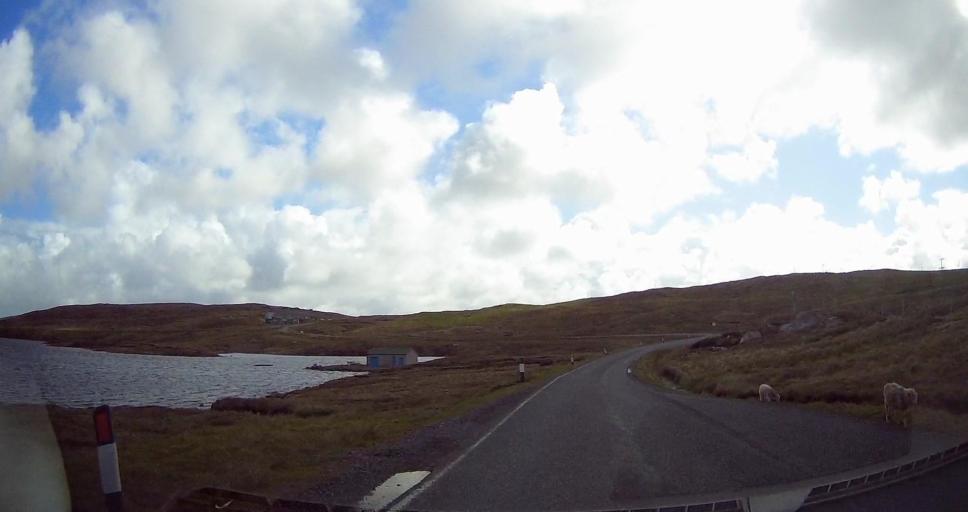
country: GB
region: Scotland
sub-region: Shetland Islands
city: Lerwick
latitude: 60.4868
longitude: -1.3973
